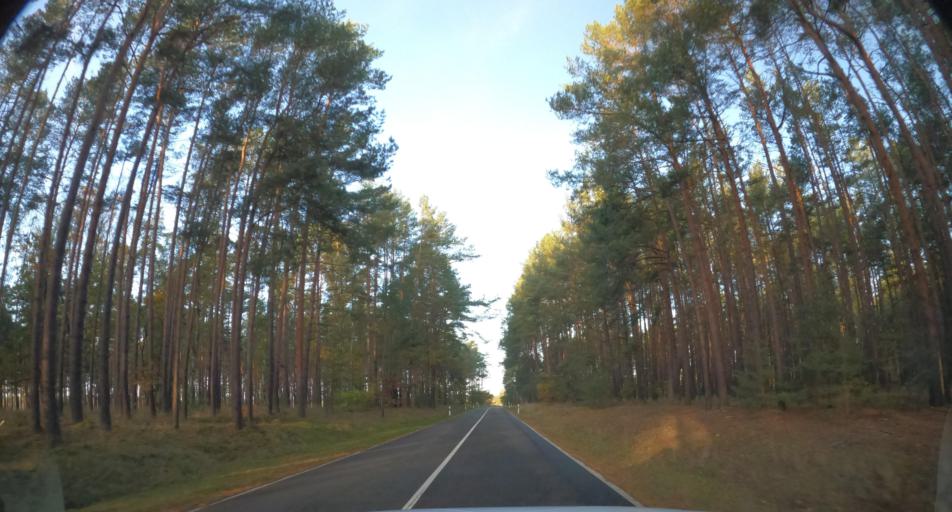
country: DE
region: Mecklenburg-Vorpommern
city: Ahlbeck
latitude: 53.6800
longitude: 14.1785
